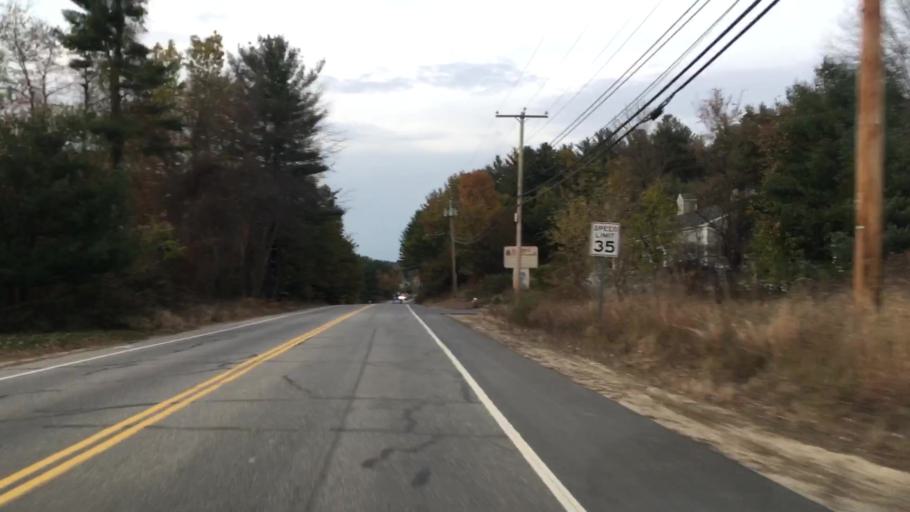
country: US
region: New Hampshire
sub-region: Hillsborough County
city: Milford
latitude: 42.8222
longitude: -71.6463
